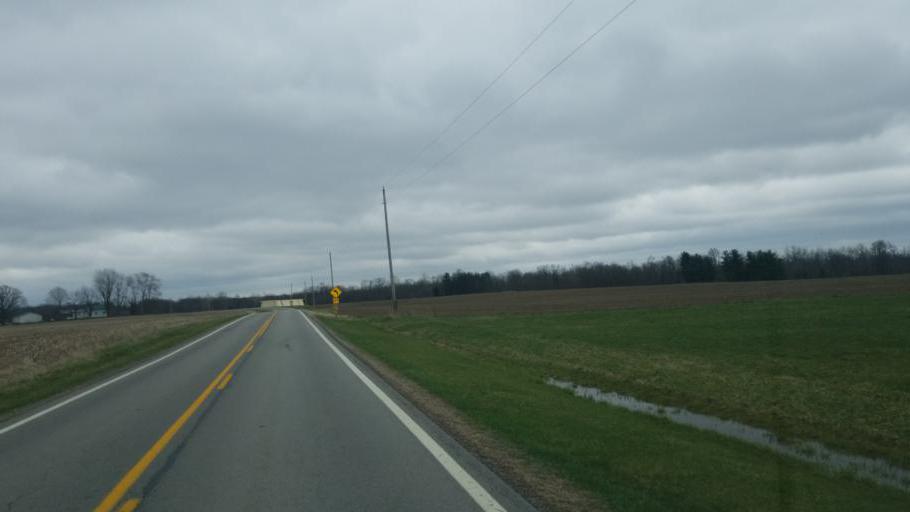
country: US
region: Ohio
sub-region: Hardin County
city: Forest
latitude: 40.6848
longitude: -83.3889
